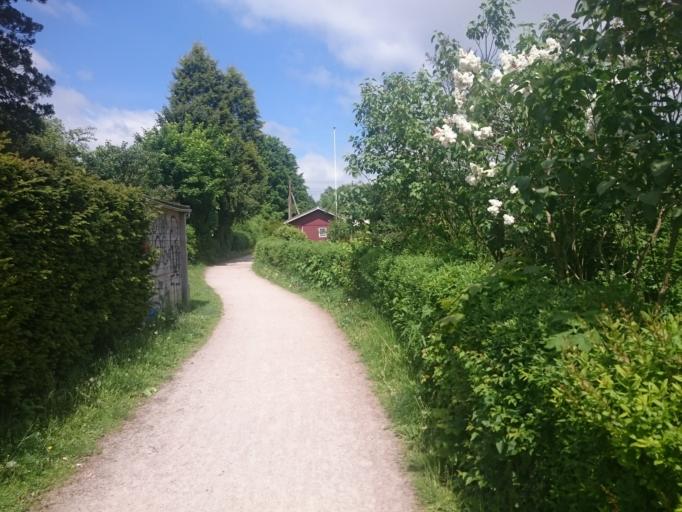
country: DE
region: Hamburg
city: Stellingen
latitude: 53.5870
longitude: 9.9512
